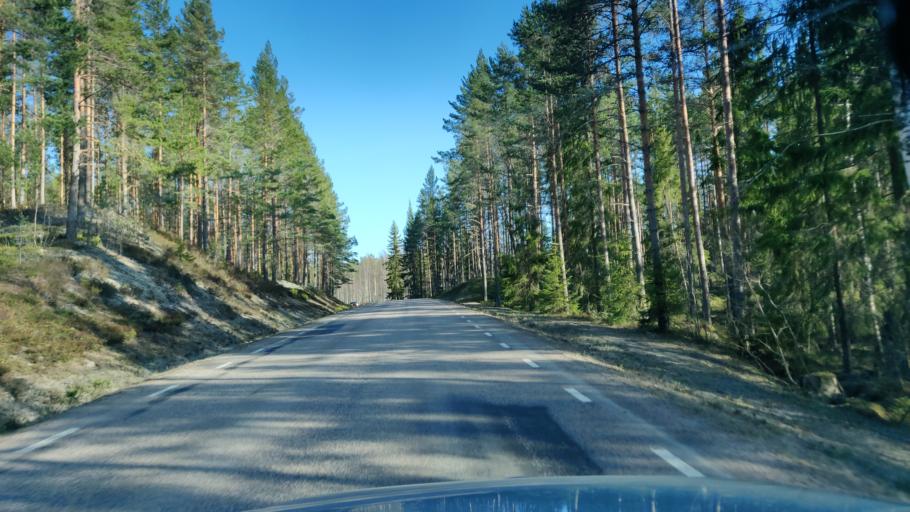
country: SE
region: Vaermland
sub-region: Sunne Kommun
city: Sunne
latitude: 59.9876
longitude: 13.3144
